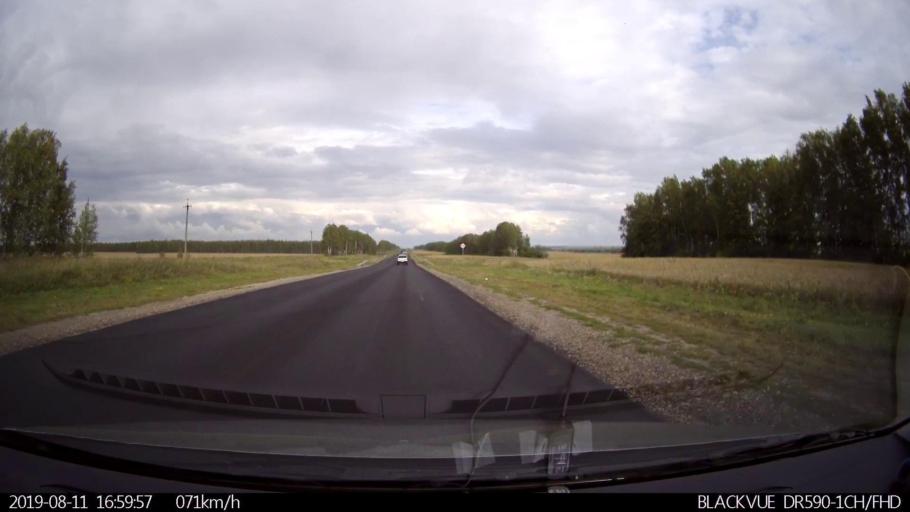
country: RU
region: Ulyanovsk
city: Mayna
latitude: 54.3114
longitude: 47.6709
